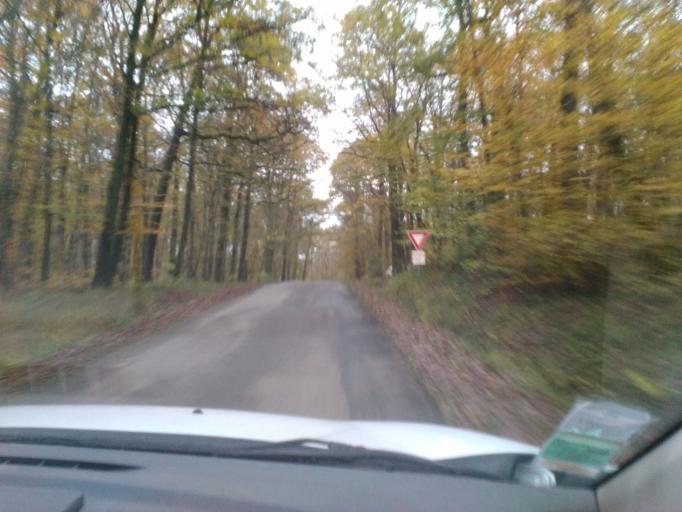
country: FR
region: Lorraine
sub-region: Departement des Vosges
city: Mirecourt
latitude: 48.2982
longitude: 6.2118
